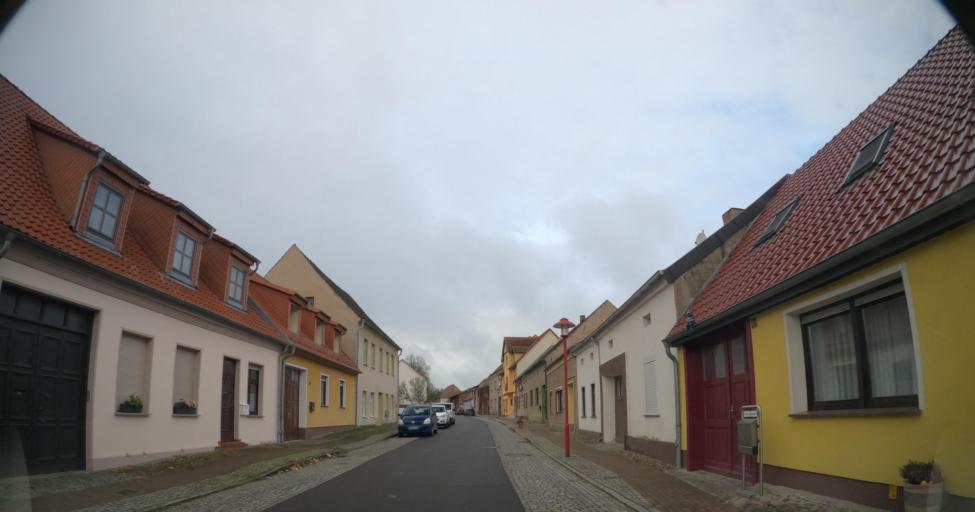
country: DE
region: Brandenburg
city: Gartz
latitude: 53.2092
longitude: 14.3939
